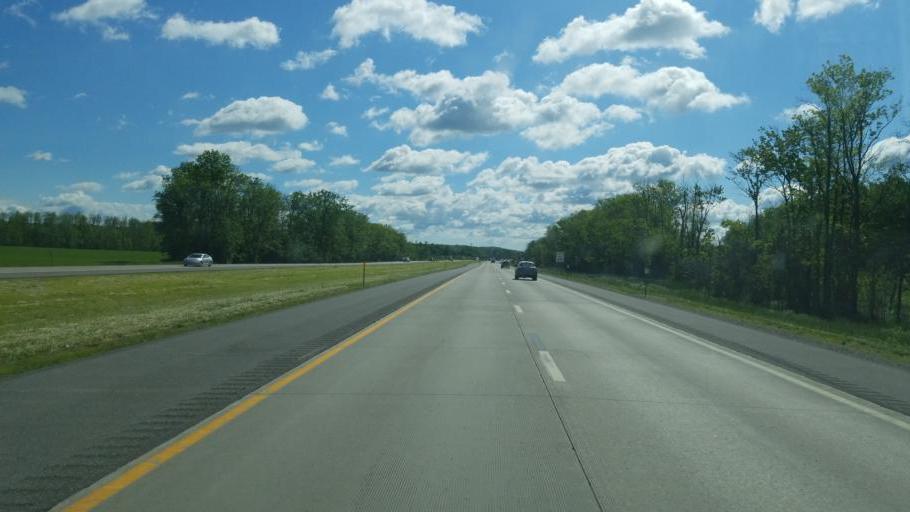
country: US
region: New York
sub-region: Onondaga County
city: Peru
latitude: 43.0885
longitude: -76.3896
